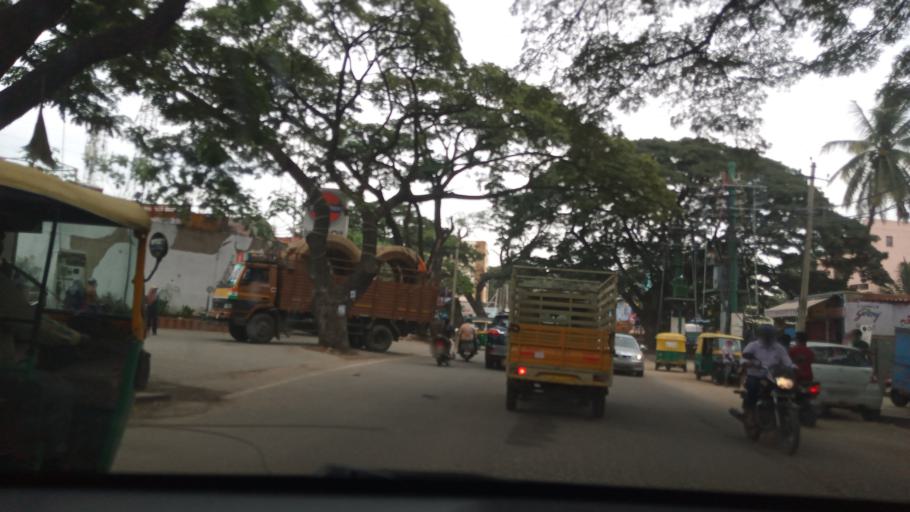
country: IN
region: Karnataka
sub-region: Bangalore Urban
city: Bangalore
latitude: 13.0200
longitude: 77.5382
